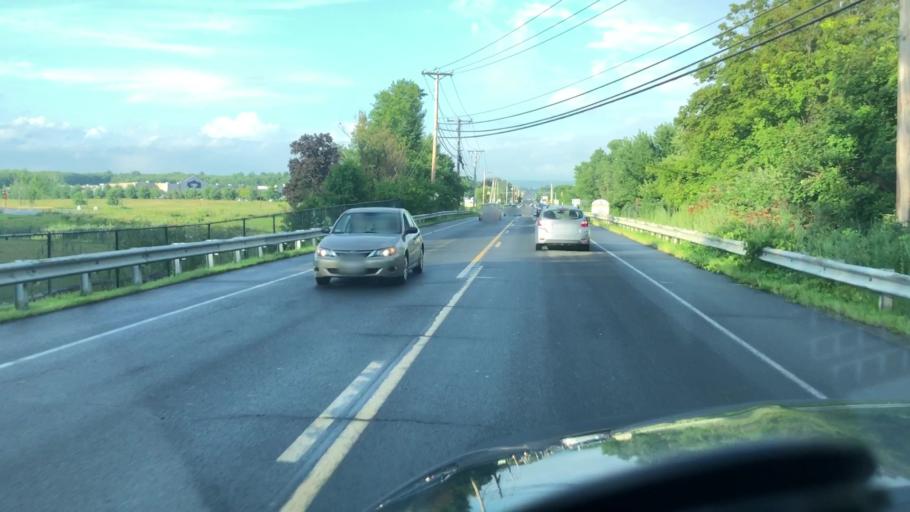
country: US
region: Massachusetts
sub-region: Hampshire County
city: Hadley
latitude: 42.3495
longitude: -72.5674
